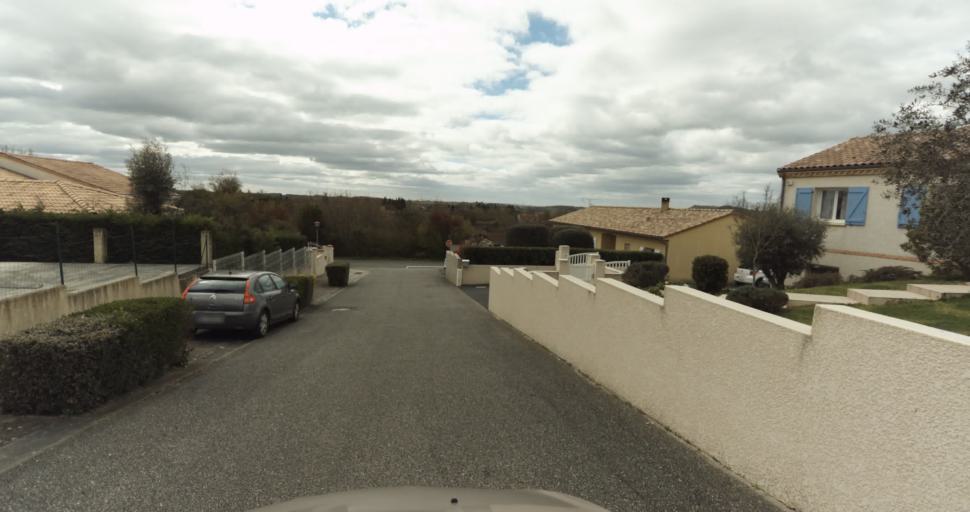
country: FR
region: Midi-Pyrenees
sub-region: Departement du Tarn
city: Puygouzon
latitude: 43.8980
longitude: 2.1760
